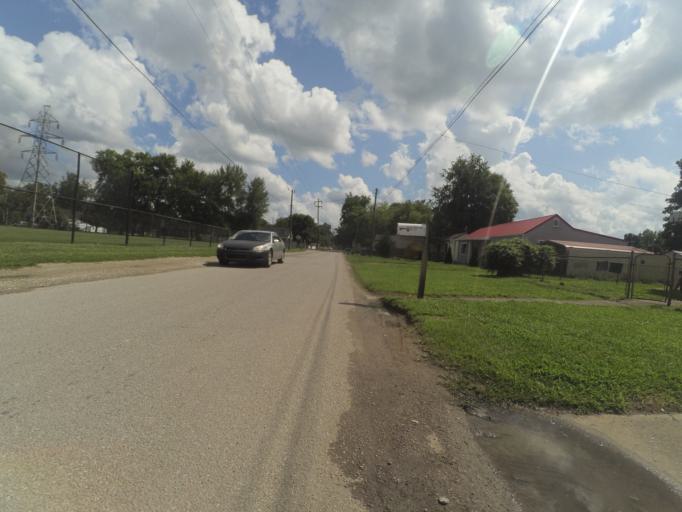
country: US
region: West Virginia
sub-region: Cabell County
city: Pea Ridge
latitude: 38.4172
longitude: -82.3569
